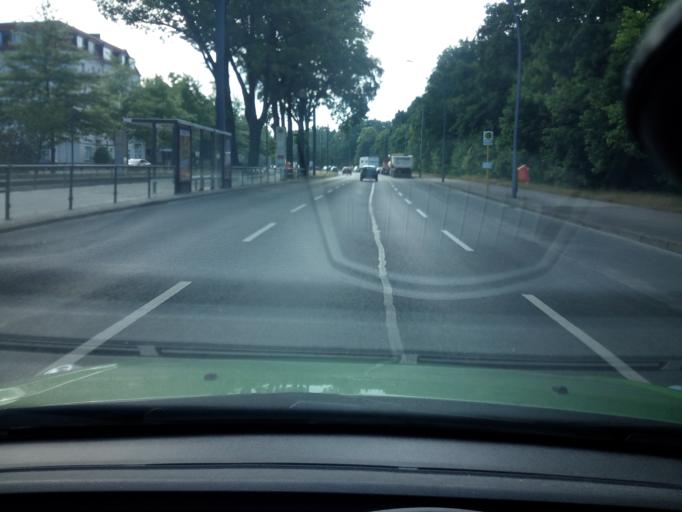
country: DE
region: Berlin
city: Adlershof
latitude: 52.4566
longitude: 13.5509
